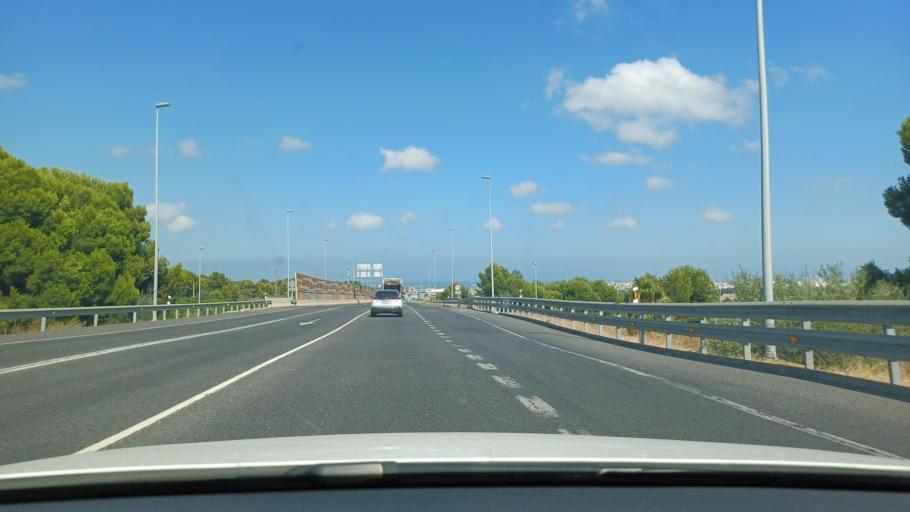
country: ES
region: Valencia
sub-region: Provincia de Castello
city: Borriol
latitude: 40.0027
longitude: -0.0767
